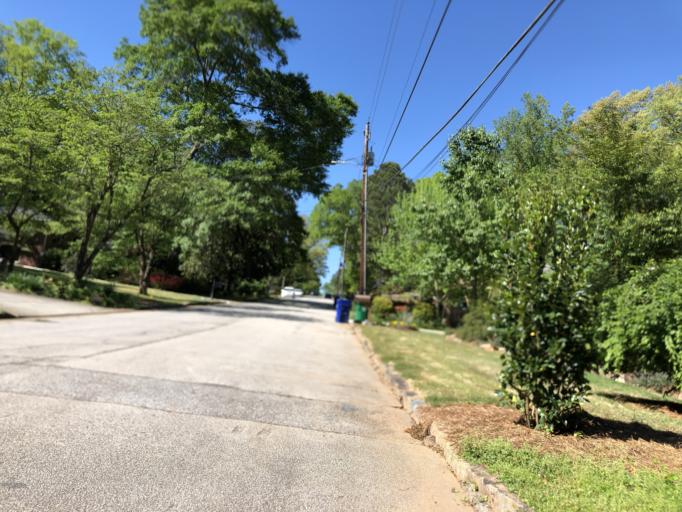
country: US
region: Georgia
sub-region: DeKalb County
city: North Decatur
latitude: 33.7971
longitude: -84.3002
